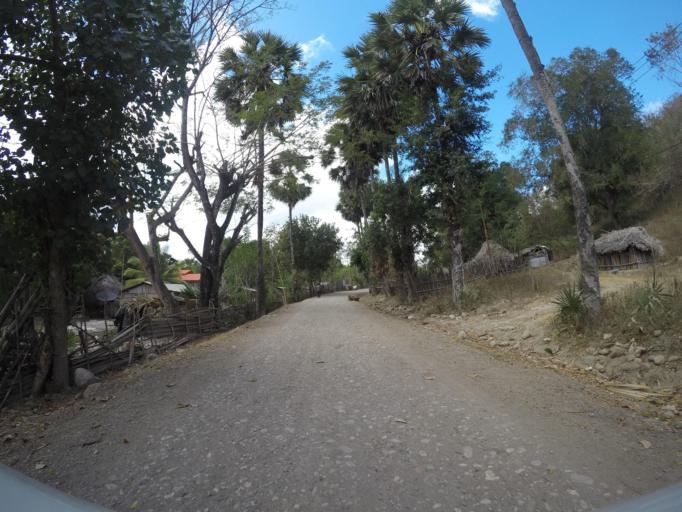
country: TL
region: Lautem
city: Lospalos
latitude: -8.4826
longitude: 126.8181
